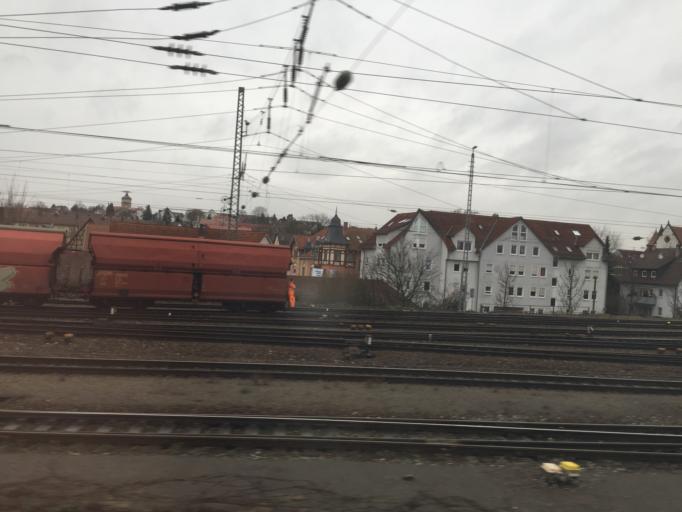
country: DE
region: Baden-Wuerttemberg
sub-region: Regierungsbezirk Stuttgart
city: Heilbronn
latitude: 49.1322
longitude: 9.1956
